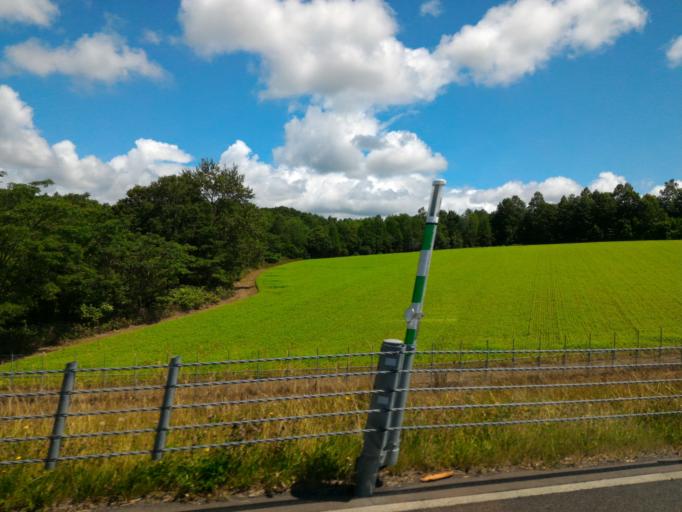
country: JP
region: Hokkaido
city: Nayoro
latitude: 44.4094
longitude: 142.4061
